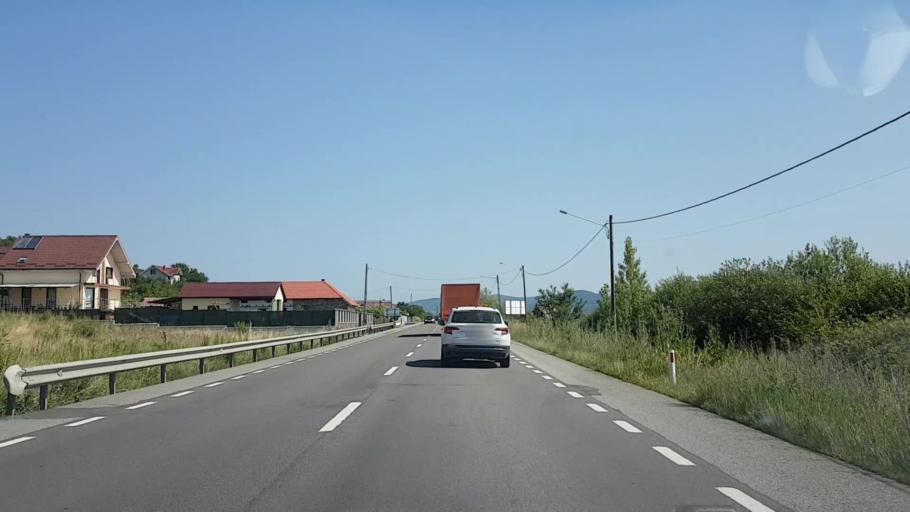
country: RO
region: Bistrita-Nasaud
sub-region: Comuna Sieu-Odorhei
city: Sieu-Odorhei
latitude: 47.1340
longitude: 24.3093
